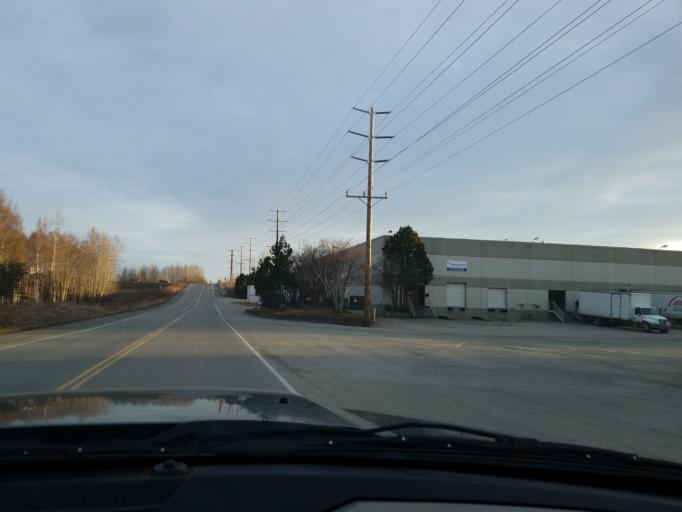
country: US
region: Alaska
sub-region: Anchorage Municipality
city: Anchorage
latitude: 61.1702
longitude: -149.9129
